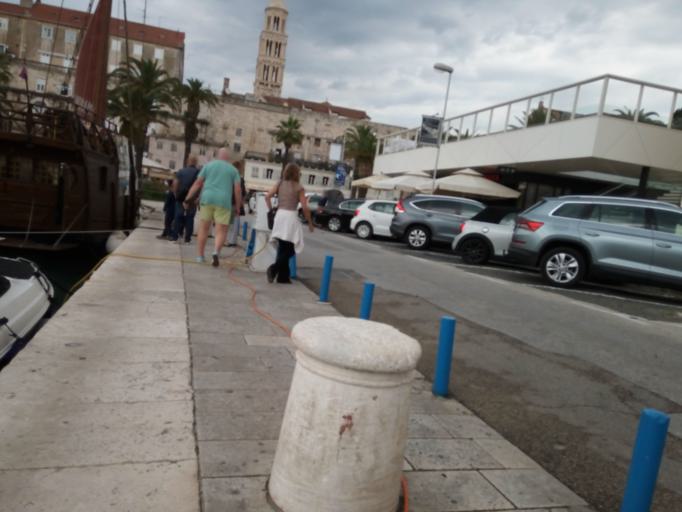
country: HR
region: Splitsko-Dalmatinska
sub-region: Grad Split
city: Split
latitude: 43.5069
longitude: 16.4393
